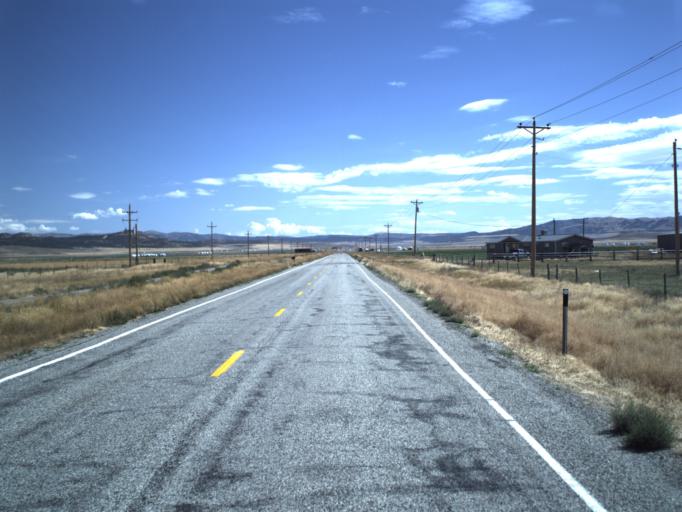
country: US
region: Idaho
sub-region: Oneida County
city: Malad City
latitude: 41.9667
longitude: -112.8942
